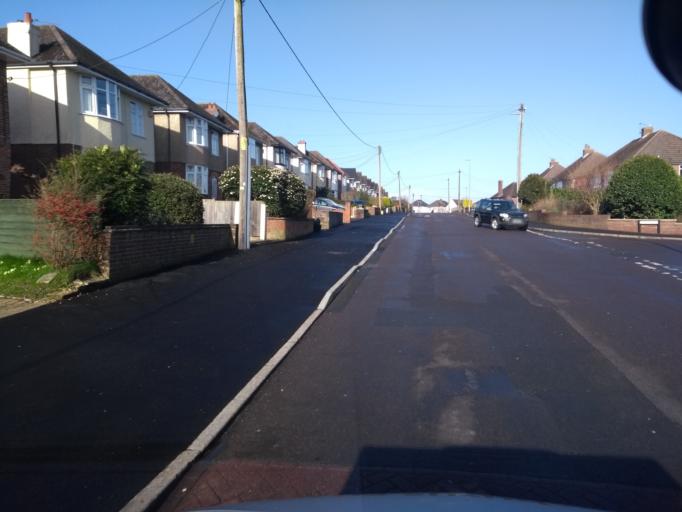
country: GB
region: England
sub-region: Somerset
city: Yeovil
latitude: 50.9562
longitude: -2.6282
